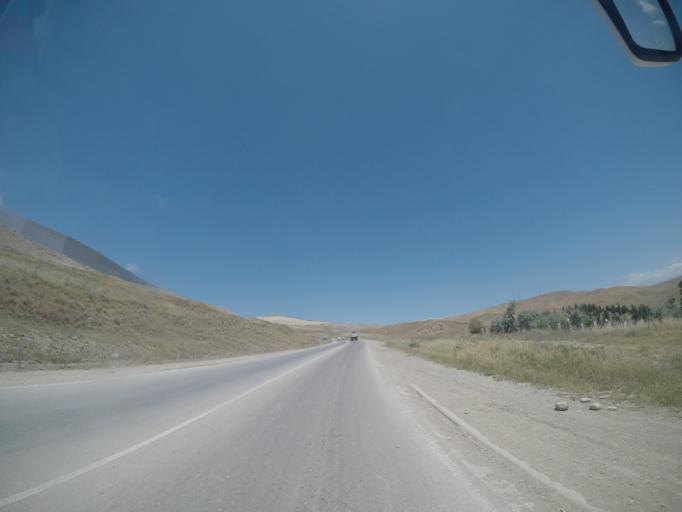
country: AZ
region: Samaxi
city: Shamakhi
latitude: 40.5576
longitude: 48.7556
